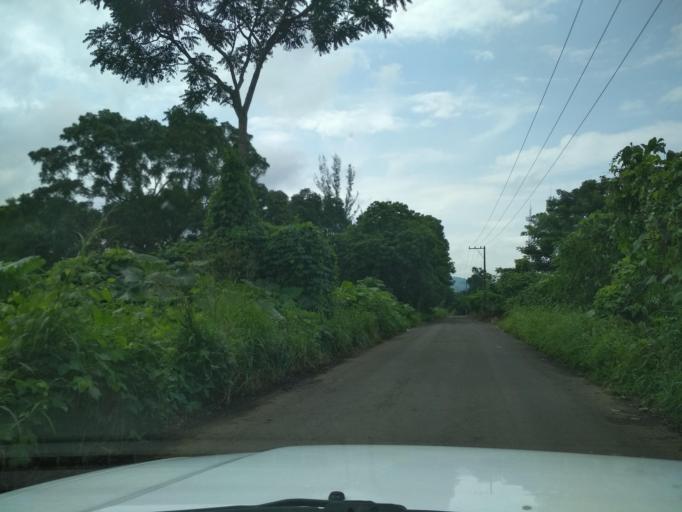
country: MX
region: Veracruz
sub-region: San Andres Tuxtla
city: Matacapan
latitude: 18.4379
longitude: -95.1700
